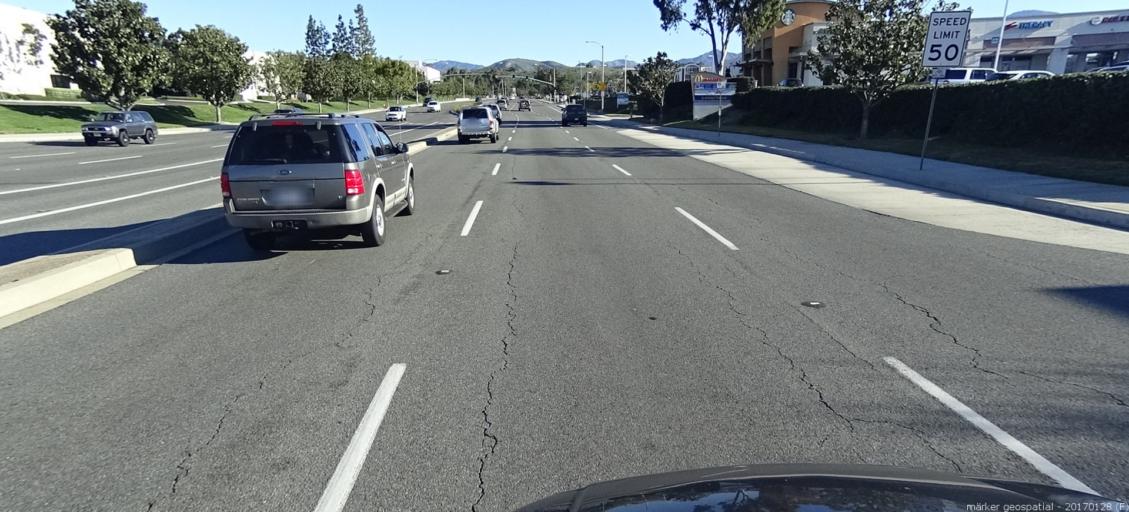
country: US
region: California
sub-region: Orange County
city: Lake Forest
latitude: 33.6554
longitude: -117.7026
